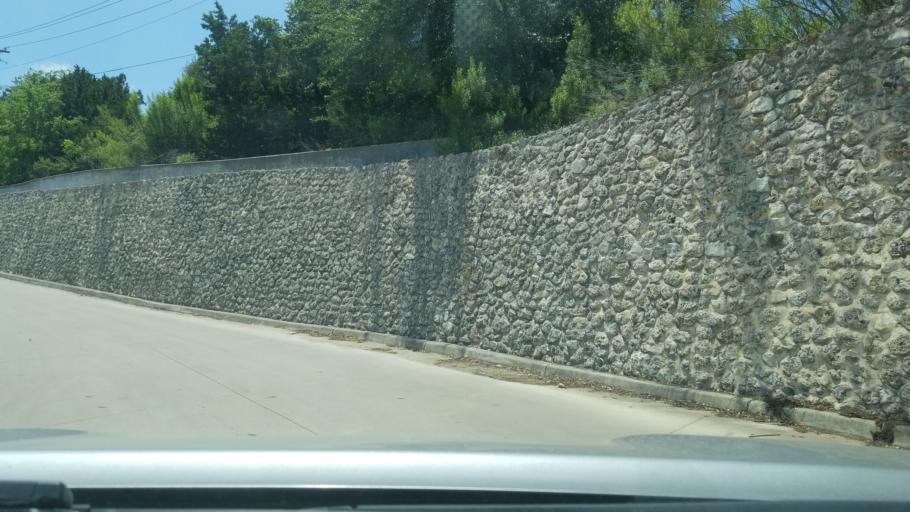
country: US
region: Texas
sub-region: Comal County
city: Bulverde
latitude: 29.7979
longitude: -98.4282
